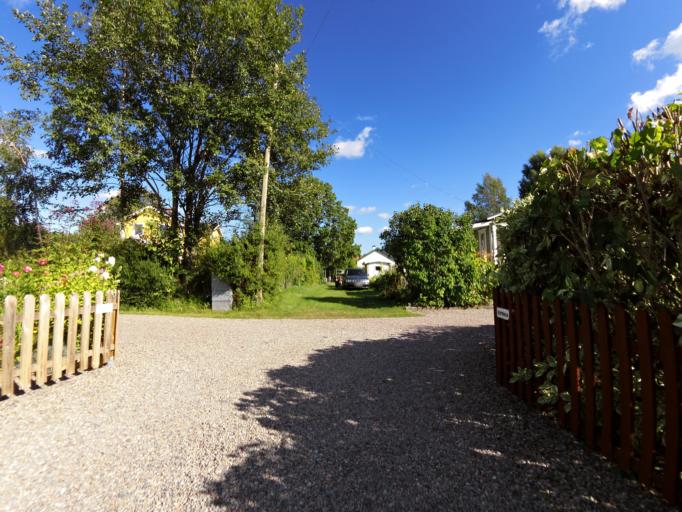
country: SE
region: Gaevleborg
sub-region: Gavle Kommun
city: Gavle
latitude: 60.7086
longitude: 17.1587
